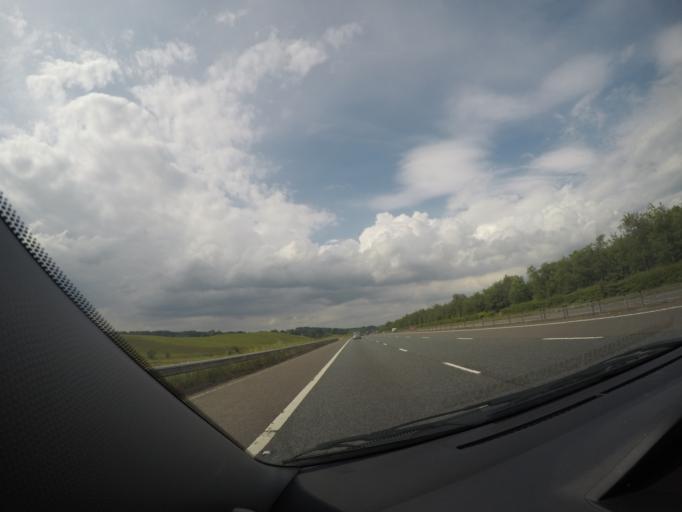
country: GB
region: Scotland
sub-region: Dumfries and Galloway
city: Lochmaben
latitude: 55.2006
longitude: -3.4116
